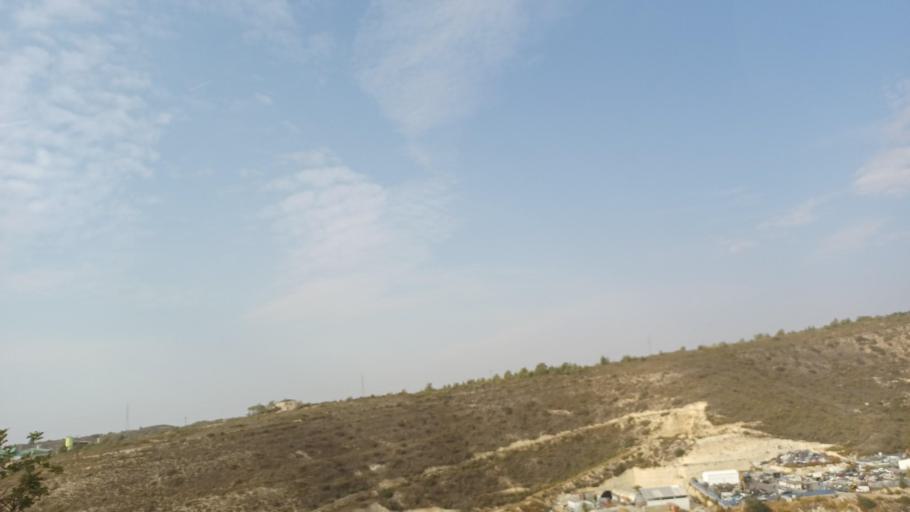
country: CY
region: Limassol
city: Ypsonas
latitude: 34.7431
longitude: 32.9474
